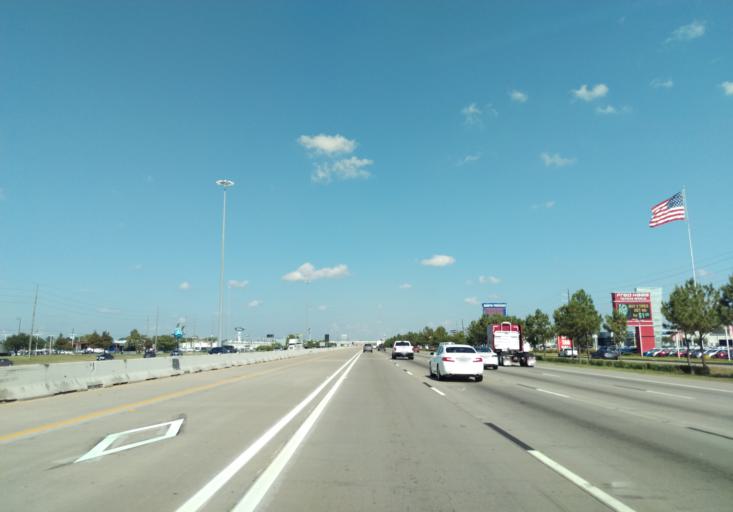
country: US
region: Texas
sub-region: Harris County
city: Spring
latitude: 30.0595
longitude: -95.4330
